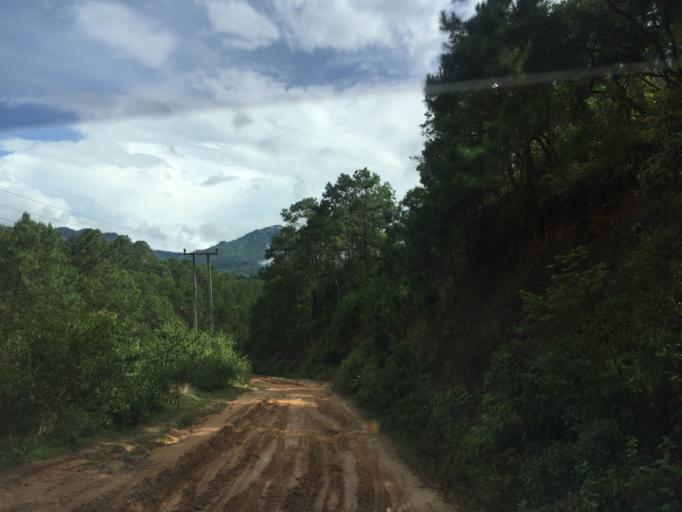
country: LA
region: Xiangkhoang
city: Muang Phonsavan
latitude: 19.3316
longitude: 103.4751
